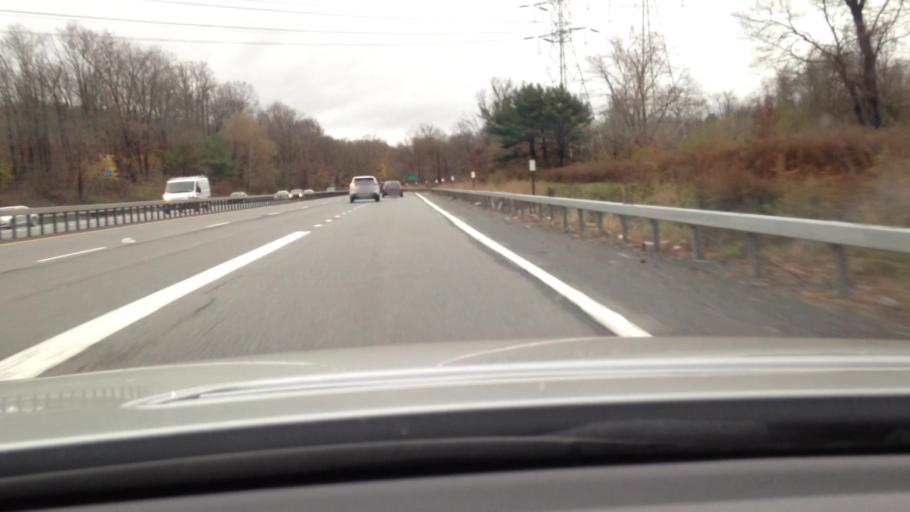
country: US
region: New York
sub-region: Westchester County
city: Briarcliff Manor
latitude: 41.1317
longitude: -73.8171
